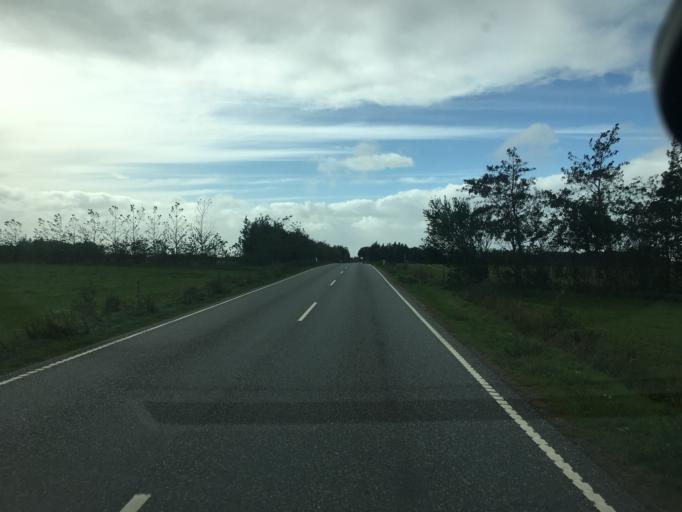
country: DK
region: South Denmark
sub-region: Tonder Kommune
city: Tonder
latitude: 55.0132
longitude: 8.8421
